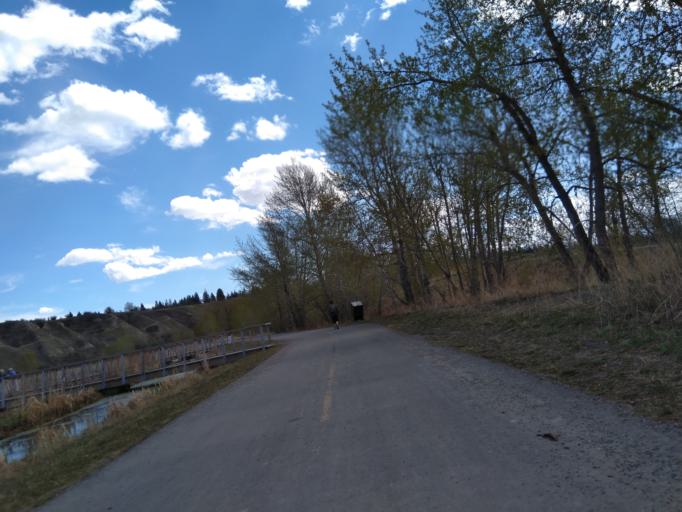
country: CA
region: Alberta
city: Calgary
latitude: 51.0873
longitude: -114.1740
